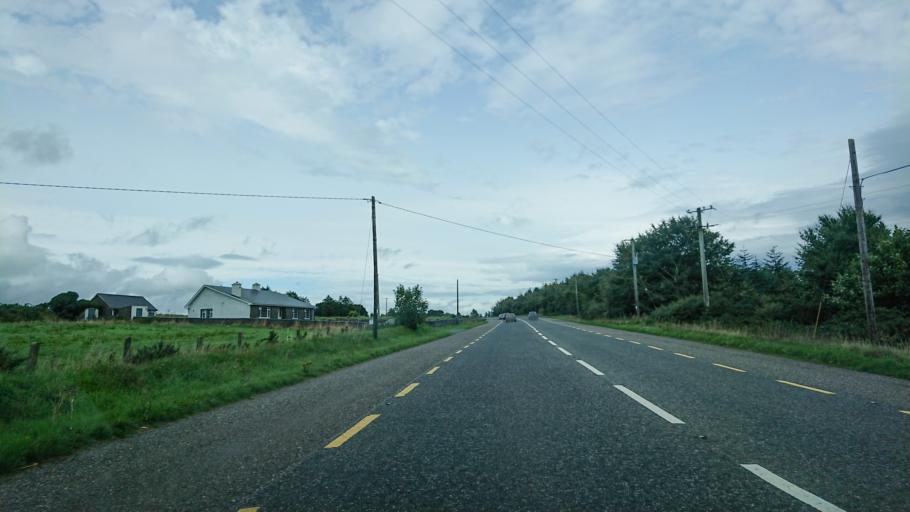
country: IE
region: Munster
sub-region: Waterford
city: Dungarvan
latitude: 52.0060
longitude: -7.7107
